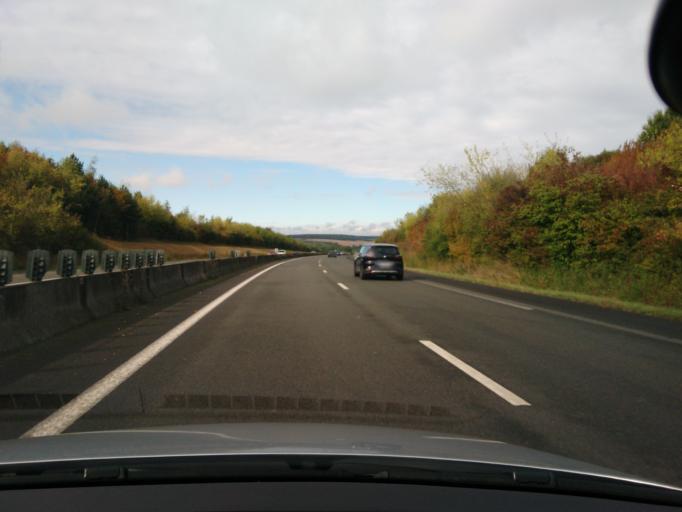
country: FR
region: Centre
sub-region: Departement d'Eure-et-Loir
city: Cherisy
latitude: 48.7496
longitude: 1.4297
